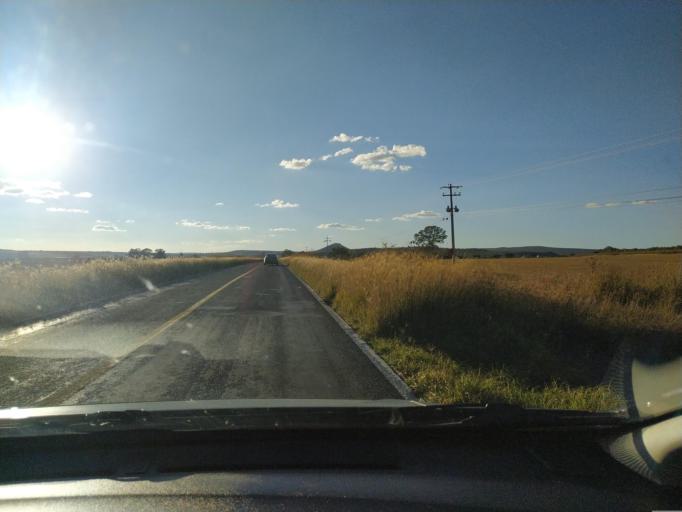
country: MX
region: Jalisco
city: San Diego de Alejandria
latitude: 21.0058
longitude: -102.0557
